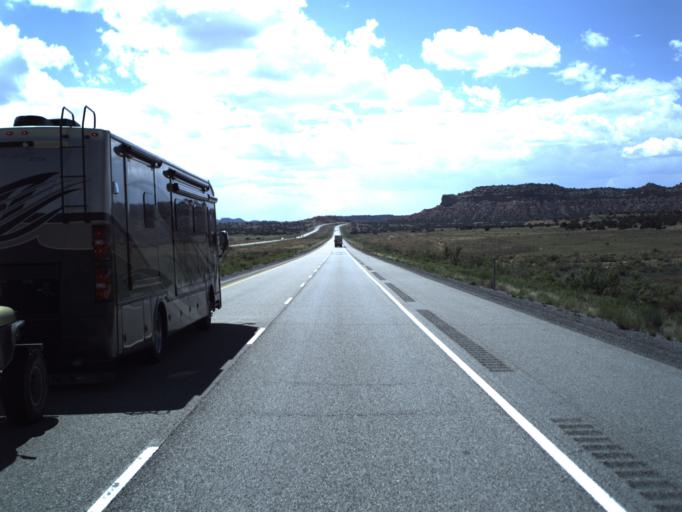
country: US
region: Utah
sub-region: Emery County
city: Castle Dale
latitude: 38.8742
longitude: -110.6779
